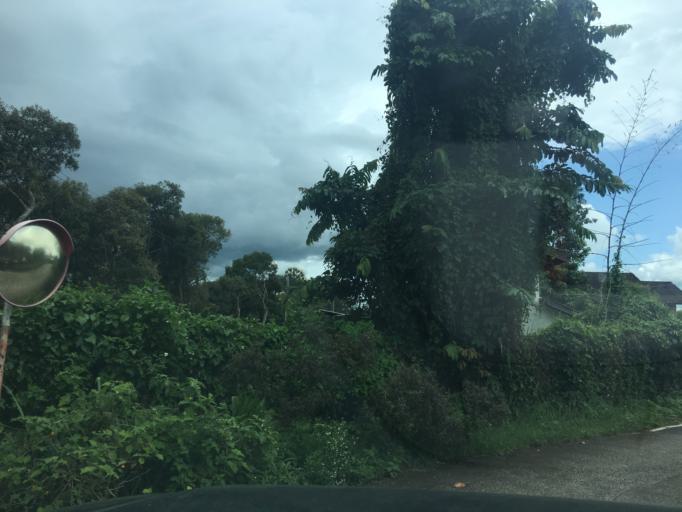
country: TH
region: Chiang Rai
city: Chiang Rai
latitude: 19.9997
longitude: 99.8648
